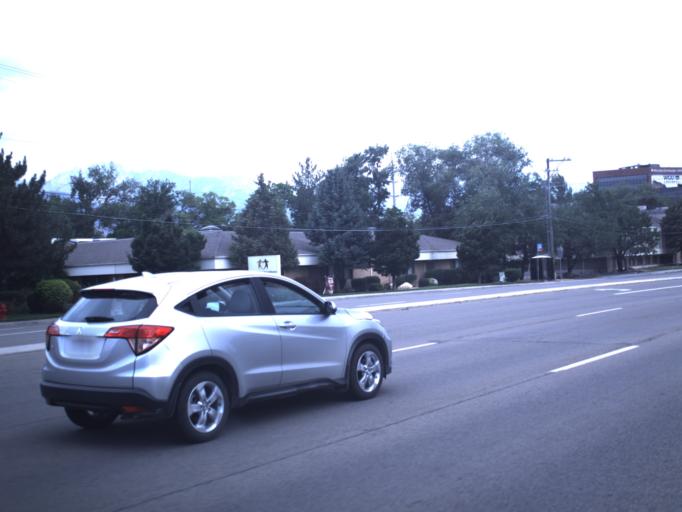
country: US
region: Utah
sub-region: Salt Lake County
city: Millcreek
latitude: 40.6887
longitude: -111.8716
